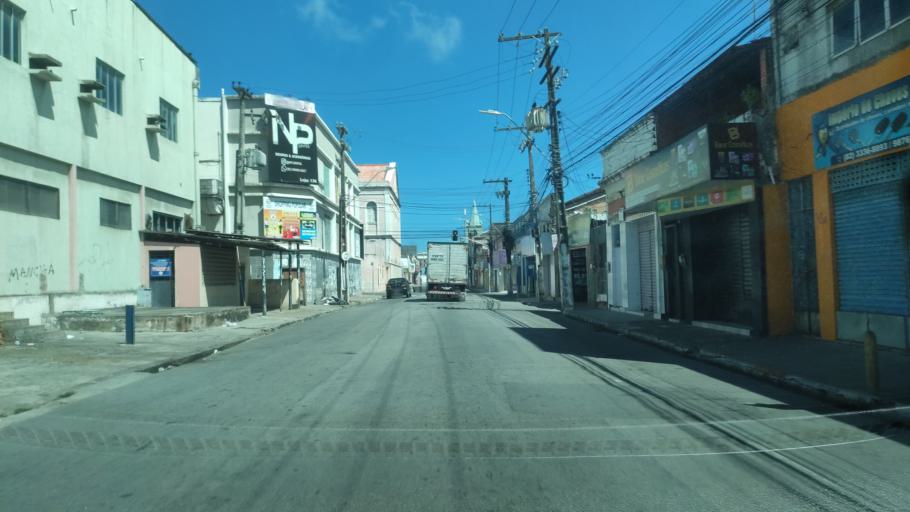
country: BR
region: Alagoas
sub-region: Maceio
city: Maceio
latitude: -9.6639
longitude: -35.7422
